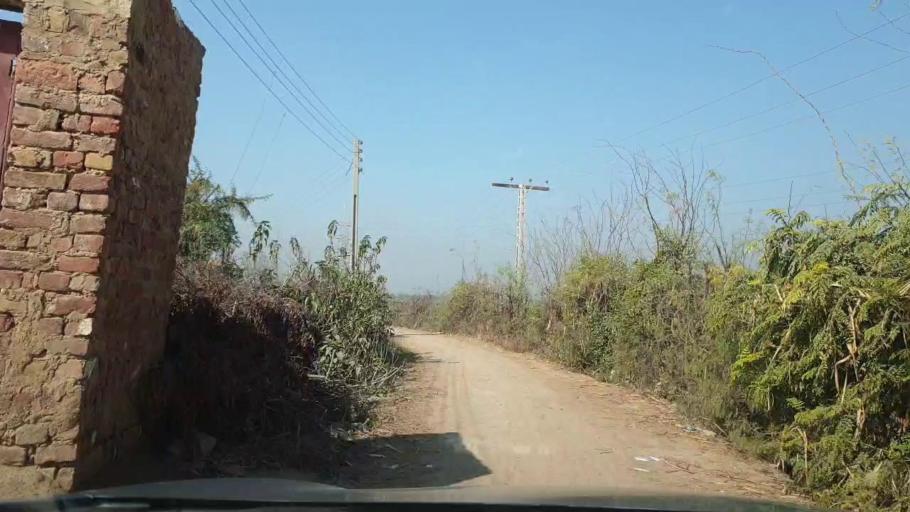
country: PK
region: Sindh
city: Tando Allahyar
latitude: 25.4680
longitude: 68.6618
